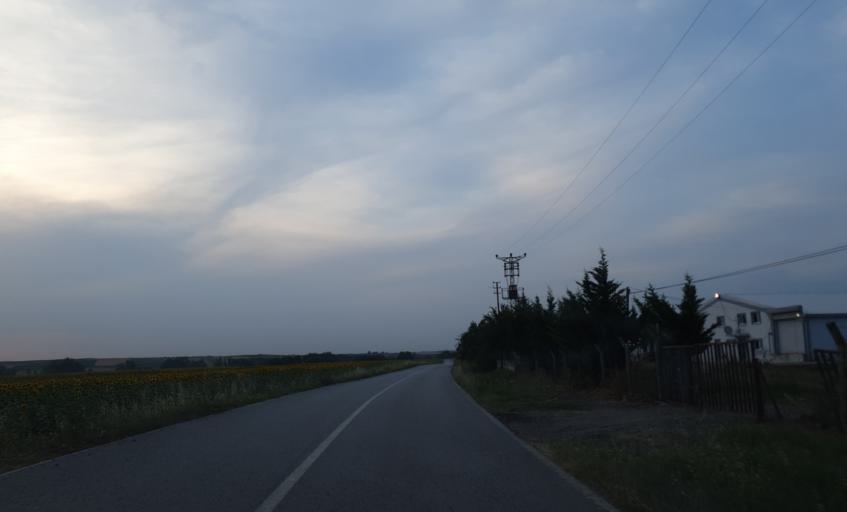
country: TR
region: Kirklareli
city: Buyukkaristiran
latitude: 41.3526
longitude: 27.6081
